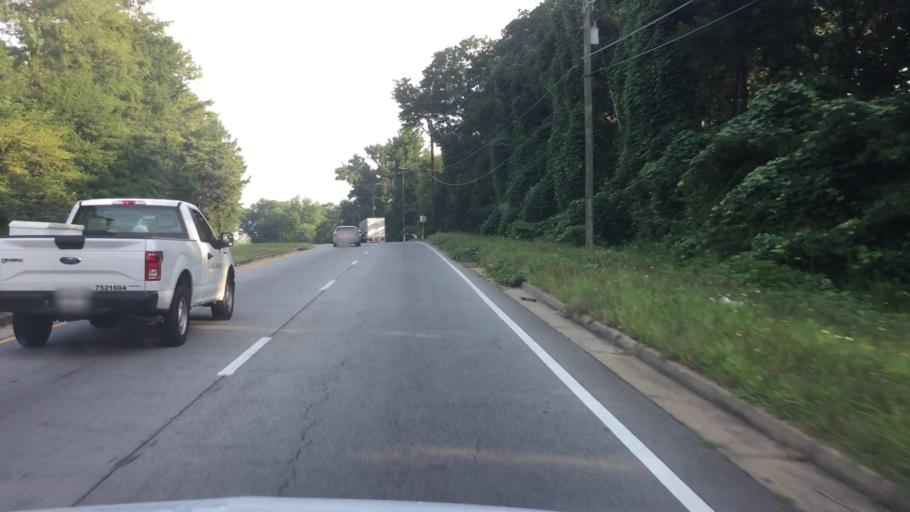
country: US
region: Georgia
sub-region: DeKalb County
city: Panthersville
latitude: 33.6852
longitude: -84.2505
